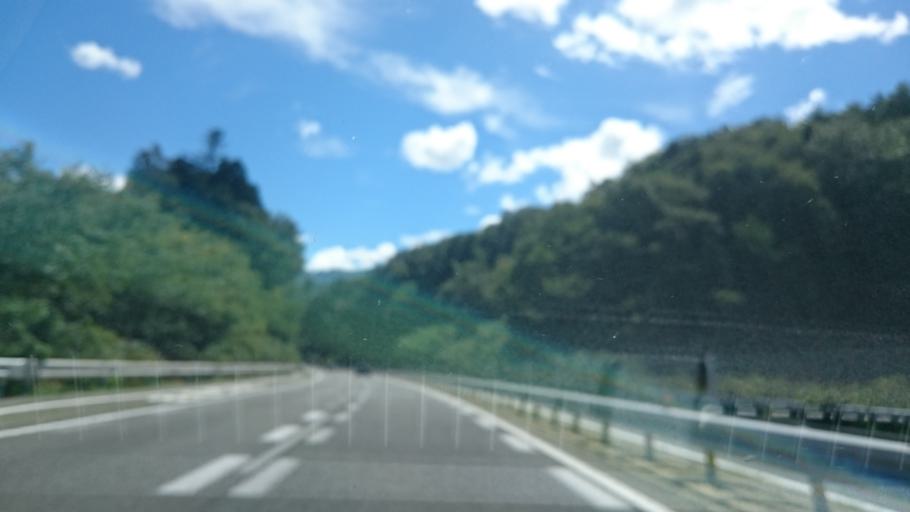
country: JP
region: Nagano
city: Iida
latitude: 35.4570
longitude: 137.7509
